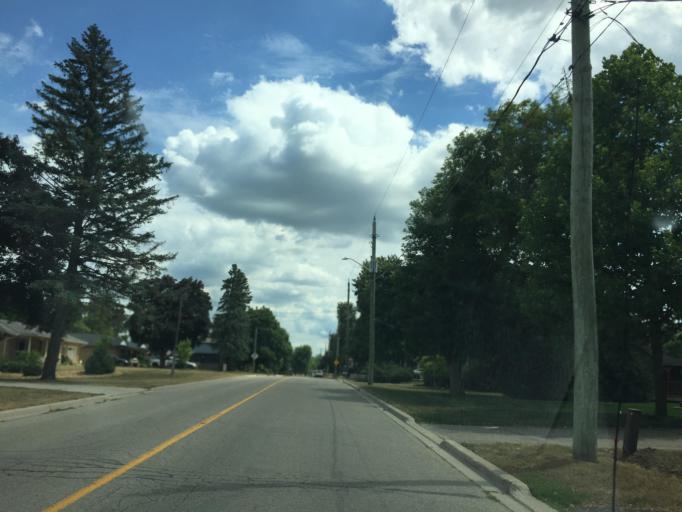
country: CA
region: Ontario
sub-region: Wellington County
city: Guelph
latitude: 43.5337
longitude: -80.3900
